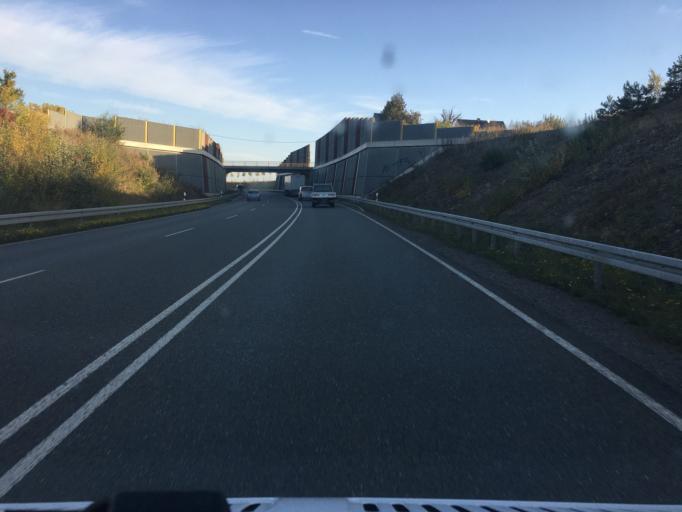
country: DE
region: Saxony
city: Hirschfeld
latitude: 50.6487
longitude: 12.4460
